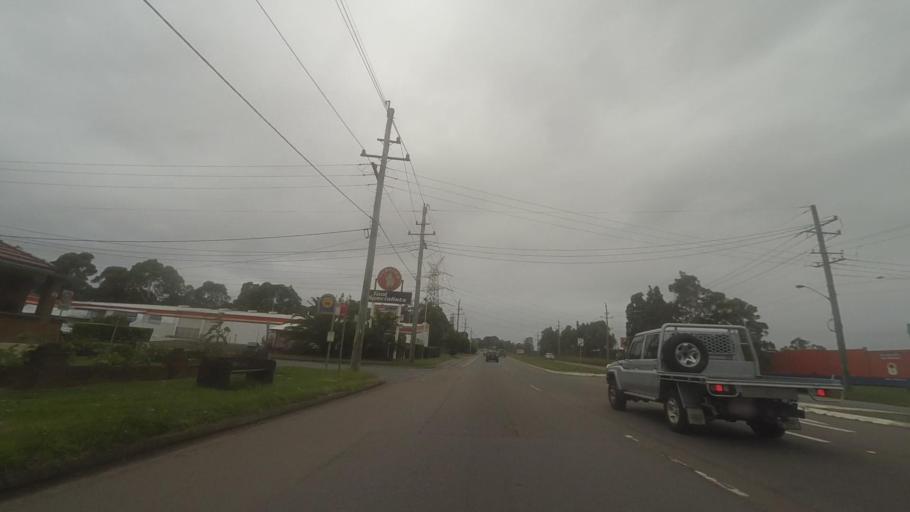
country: AU
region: New South Wales
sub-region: Newcastle
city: Mayfield West
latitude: -32.8738
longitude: 151.7121
